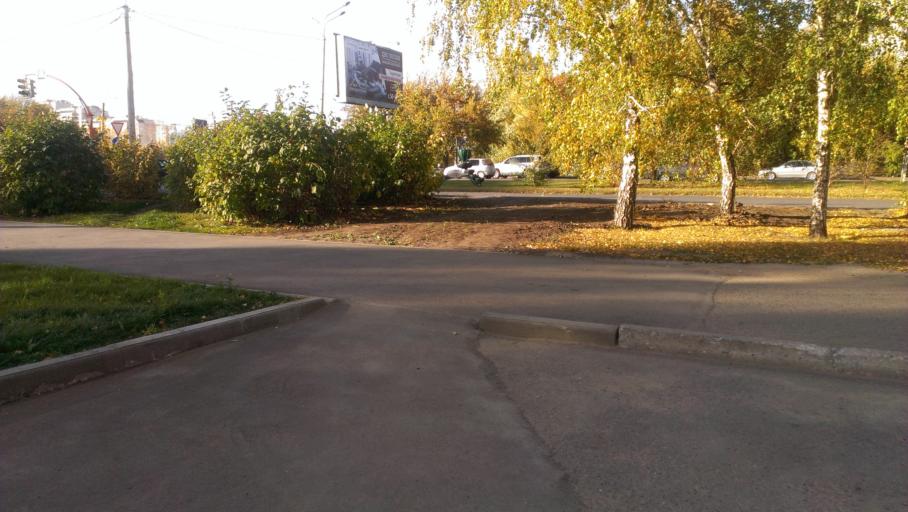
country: RU
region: Altai Krai
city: Novosilikatnyy
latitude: 53.3439
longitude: 83.6719
